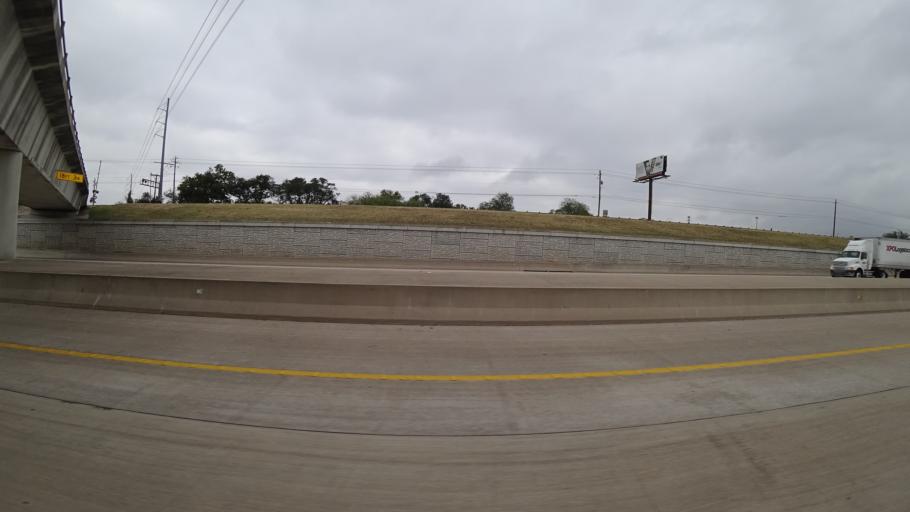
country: US
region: Texas
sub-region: Williamson County
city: Jollyville
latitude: 30.4774
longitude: -97.7614
